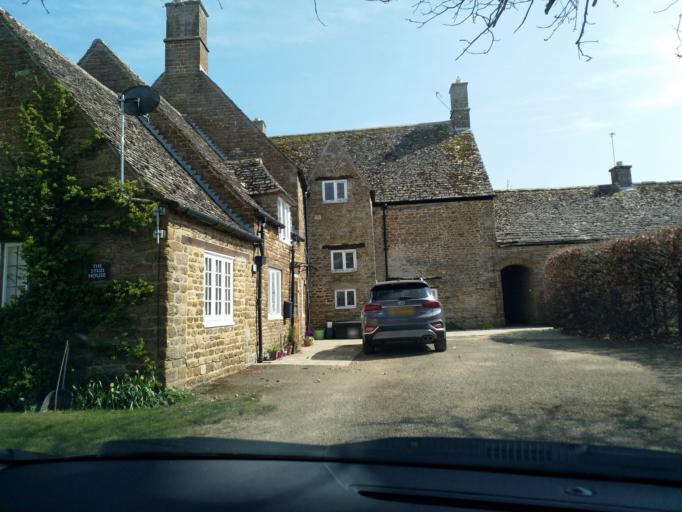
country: GB
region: England
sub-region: Oxfordshire
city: Adderbury
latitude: 52.0513
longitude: -1.2472
